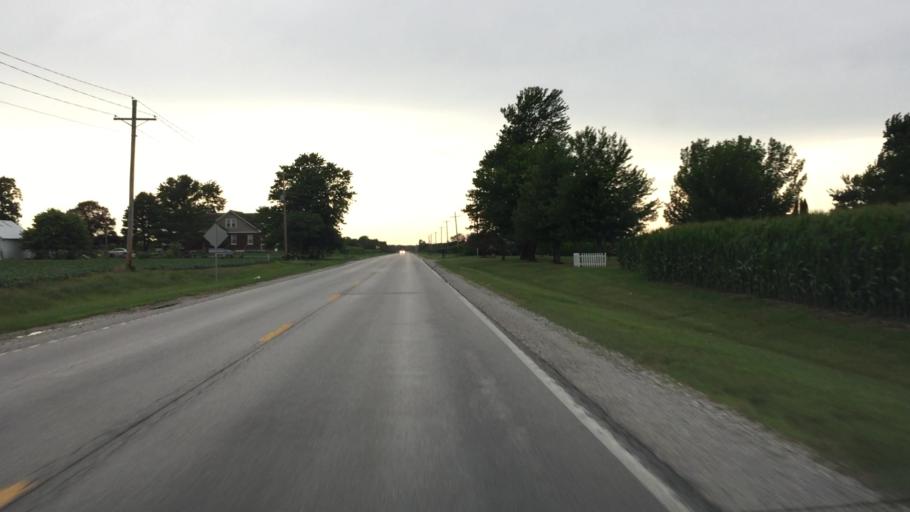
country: US
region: Illinois
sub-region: Hancock County
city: Hamilton
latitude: 40.3627
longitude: -91.3478
